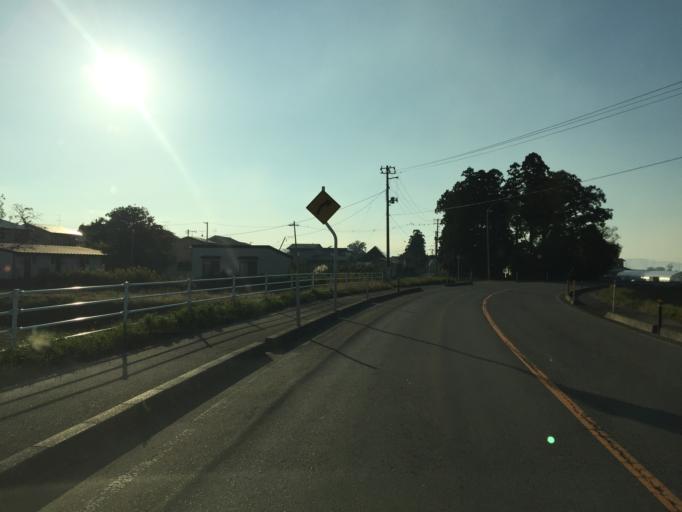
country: JP
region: Fukushima
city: Kitakata
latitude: 37.5544
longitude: 139.9050
